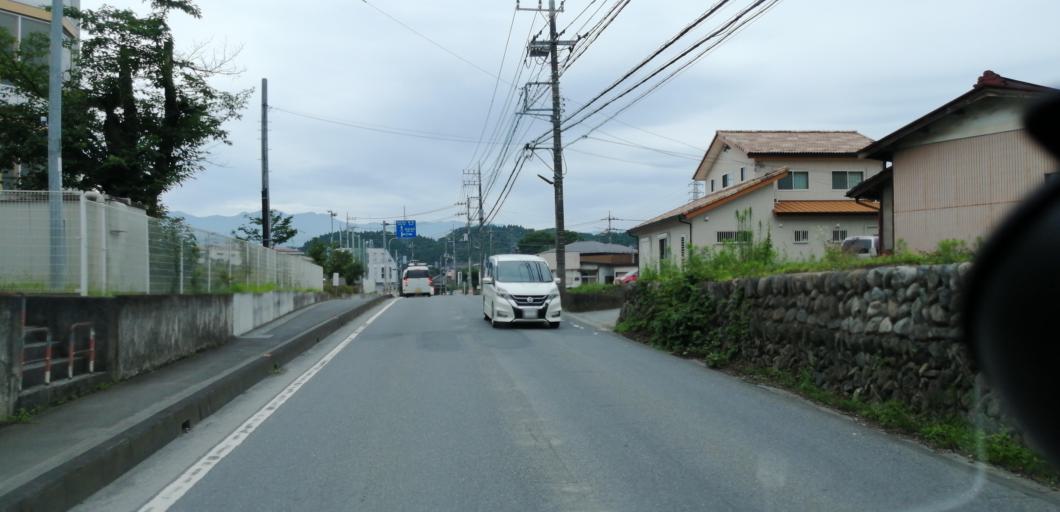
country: JP
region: Saitama
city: Chichibu
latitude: 36.0218
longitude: 139.1141
